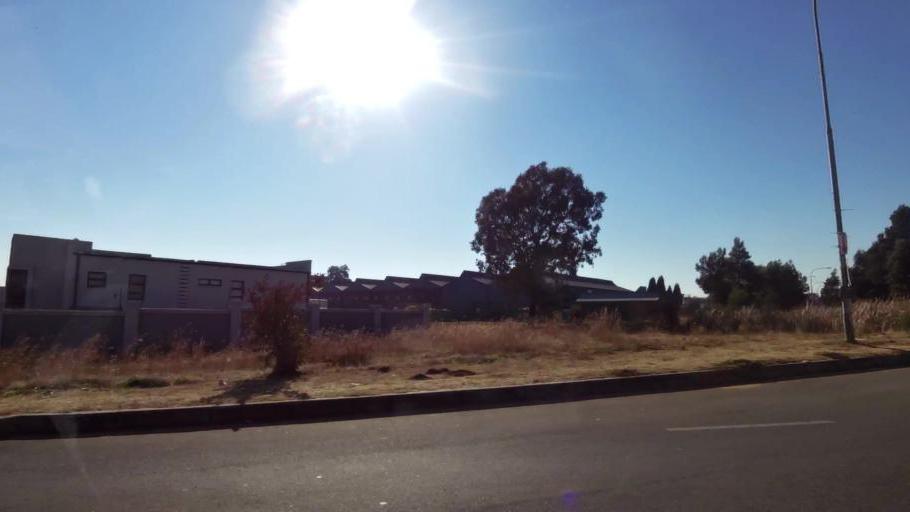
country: ZA
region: Gauteng
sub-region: City of Johannesburg Metropolitan Municipality
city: Johannesburg
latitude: -26.2394
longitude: 27.9989
